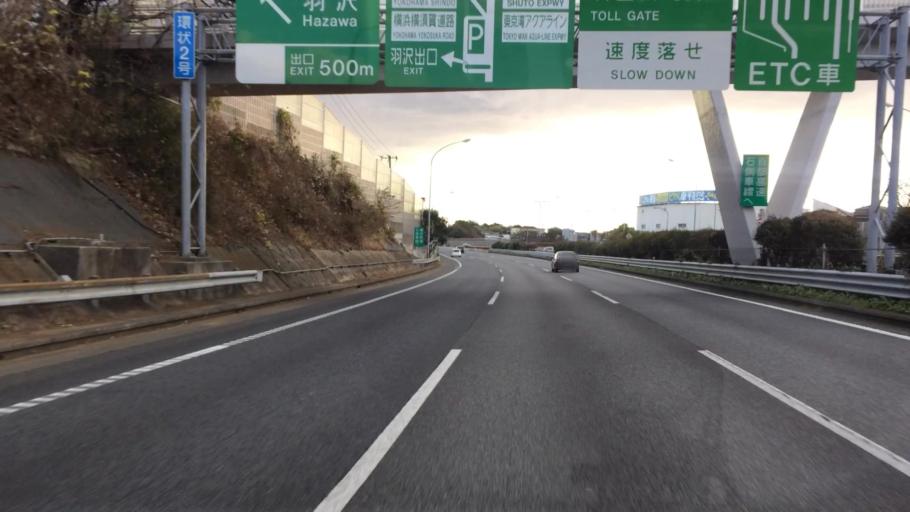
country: JP
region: Kanagawa
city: Yokohama
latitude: 35.4889
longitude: 139.5923
